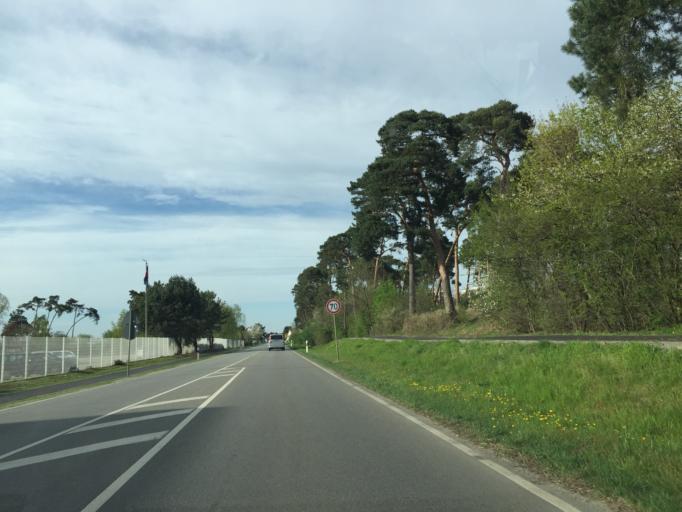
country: DE
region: Hesse
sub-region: Regierungsbezirk Darmstadt
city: Bickenbach
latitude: 49.7466
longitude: 8.6099
